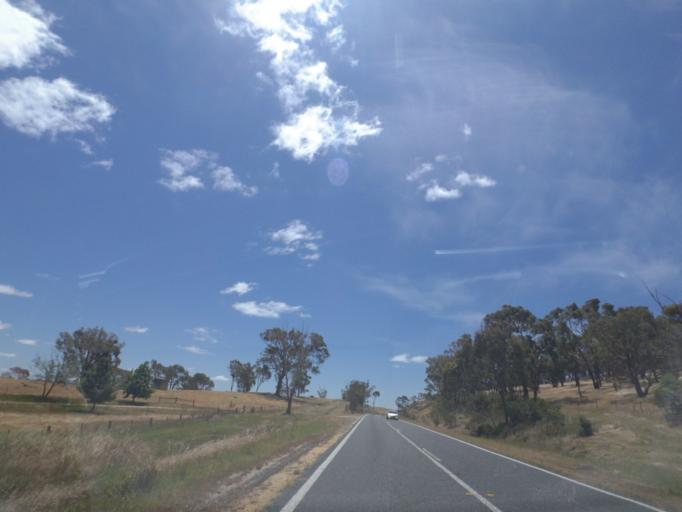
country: AU
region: Victoria
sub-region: Mount Alexander
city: Castlemaine
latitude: -37.2156
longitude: 144.1403
